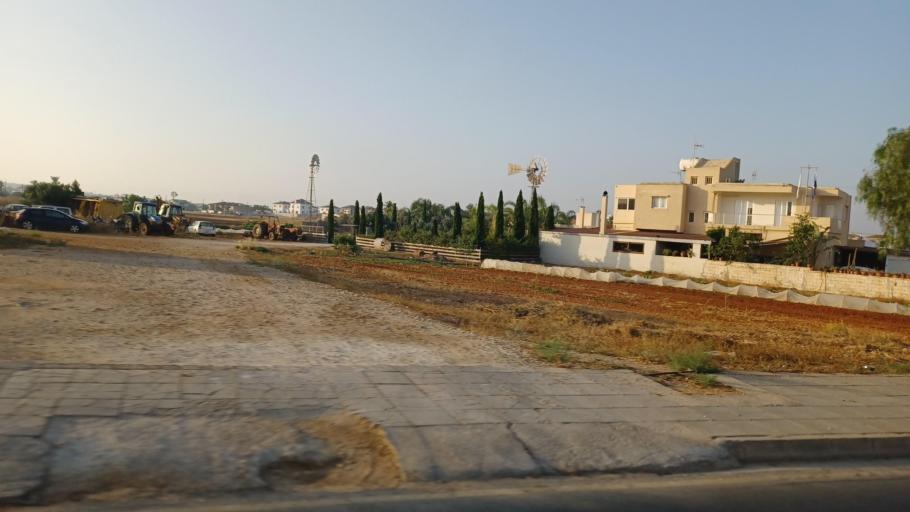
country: CY
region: Ammochostos
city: Frenaros
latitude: 35.0226
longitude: 33.9474
